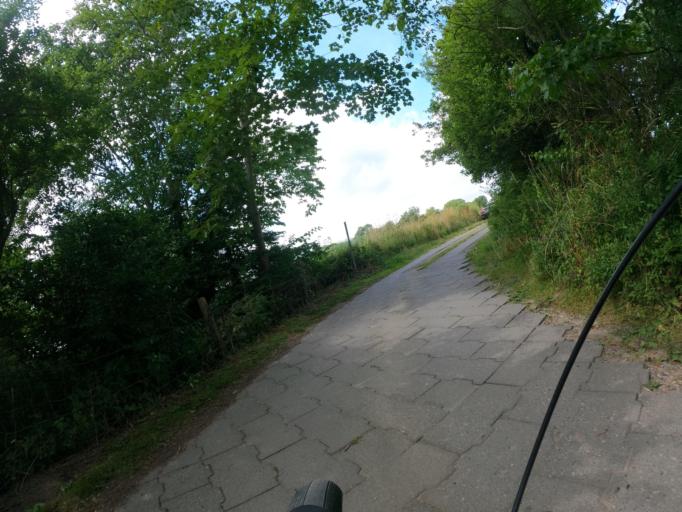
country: DE
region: Schleswig-Holstein
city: Steinberg
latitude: 54.7940
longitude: 9.7929
